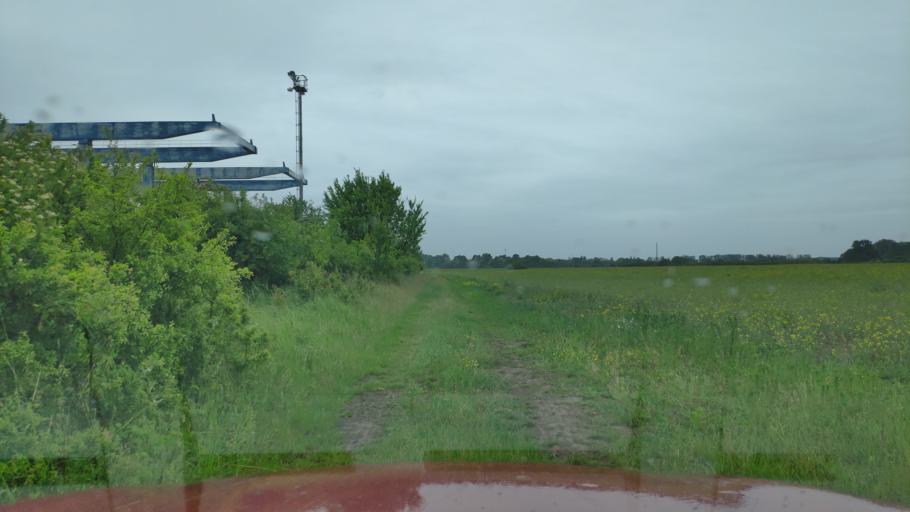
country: SK
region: Kosicky
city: Cierna nad Tisou
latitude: 48.4137
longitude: 22.0204
